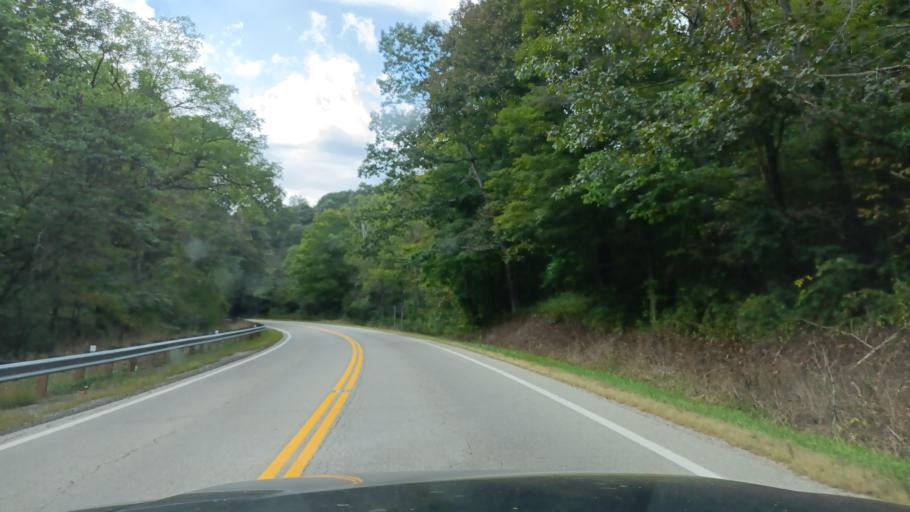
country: US
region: Ohio
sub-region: Vinton County
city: McArthur
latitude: 39.2368
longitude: -82.3302
